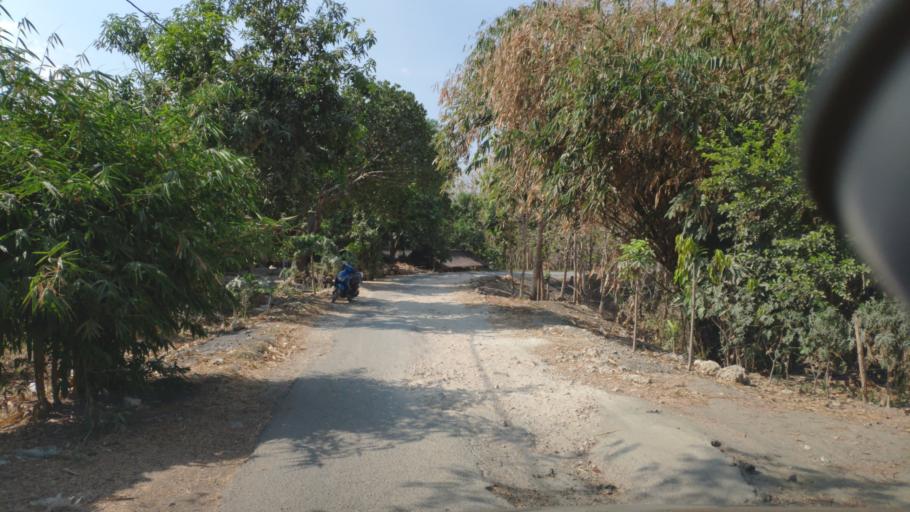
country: ID
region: Central Java
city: Gesik
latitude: -7.0461
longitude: 111.3363
